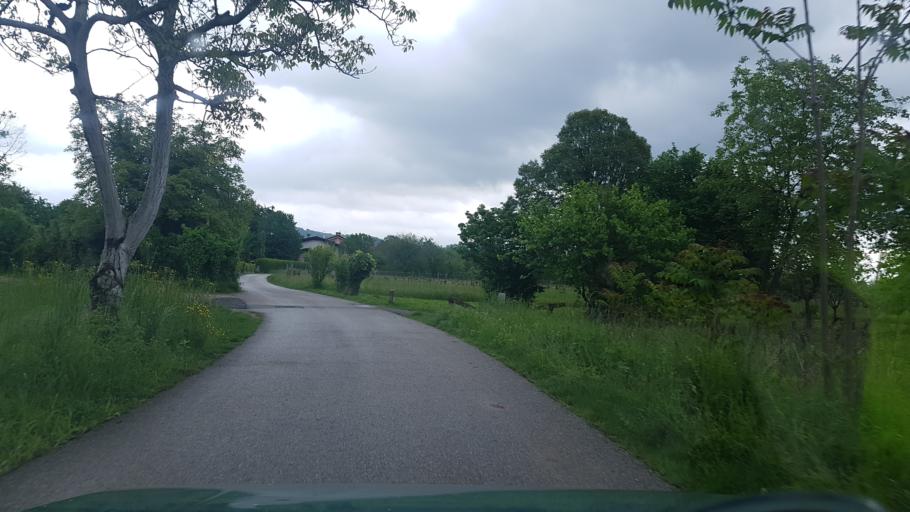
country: IT
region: Friuli Venezia Giulia
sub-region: Provincia di Gorizia
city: Mossa
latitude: 45.9334
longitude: 13.5579
